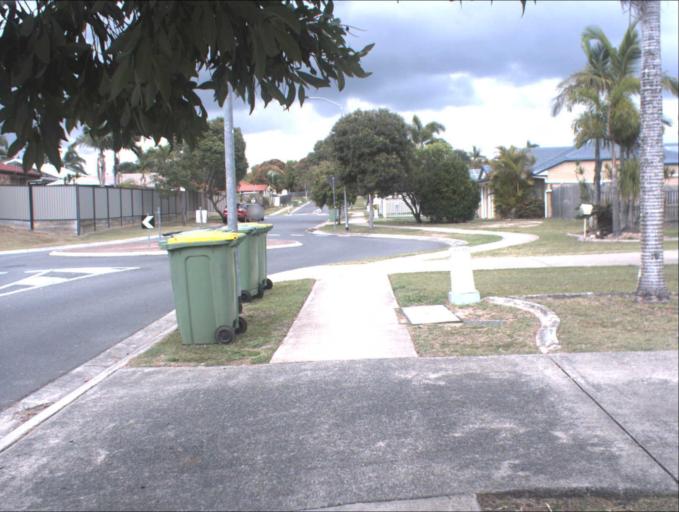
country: AU
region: Queensland
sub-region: Logan
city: Park Ridge South
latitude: -27.6778
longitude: 153.0434
